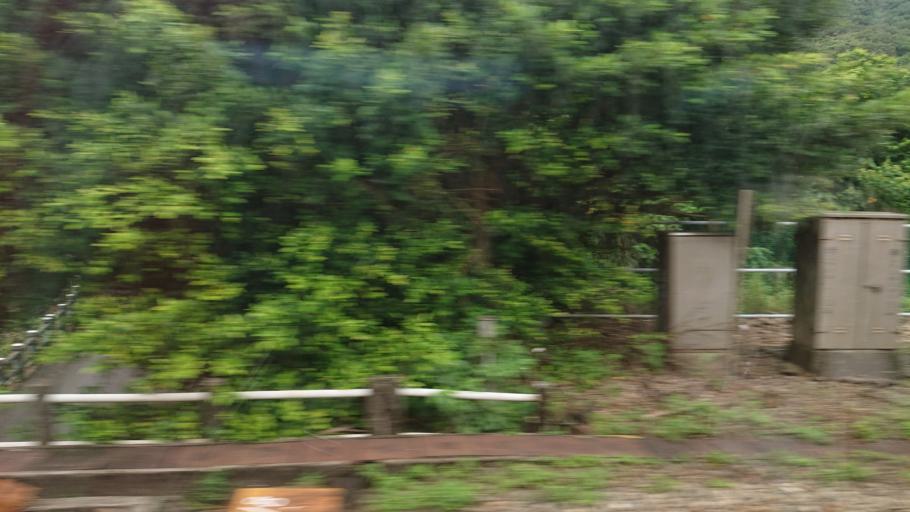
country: TW
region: Taiwan
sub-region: Keelung
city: Keelung
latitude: 24.9639
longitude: 121.9209
